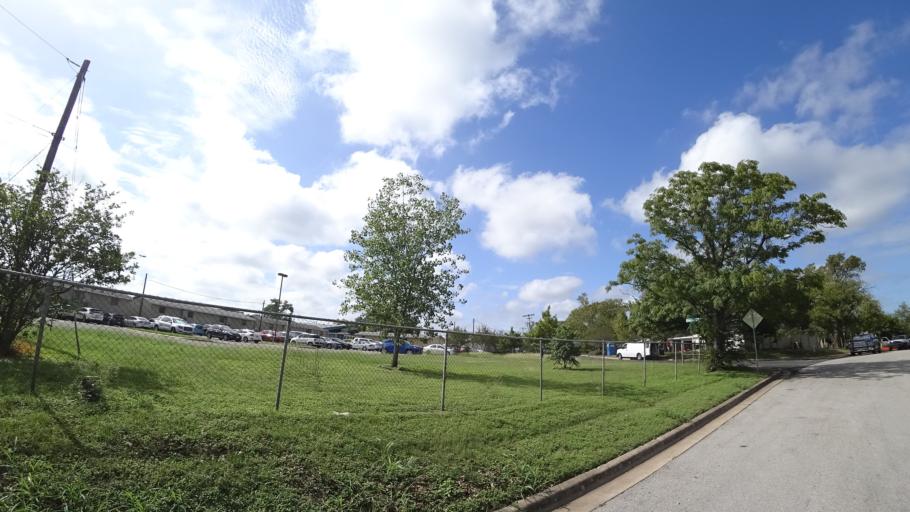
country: US
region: Texas
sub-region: Travis County
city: West Lake Hills
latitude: 30.3538
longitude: -97.7370
